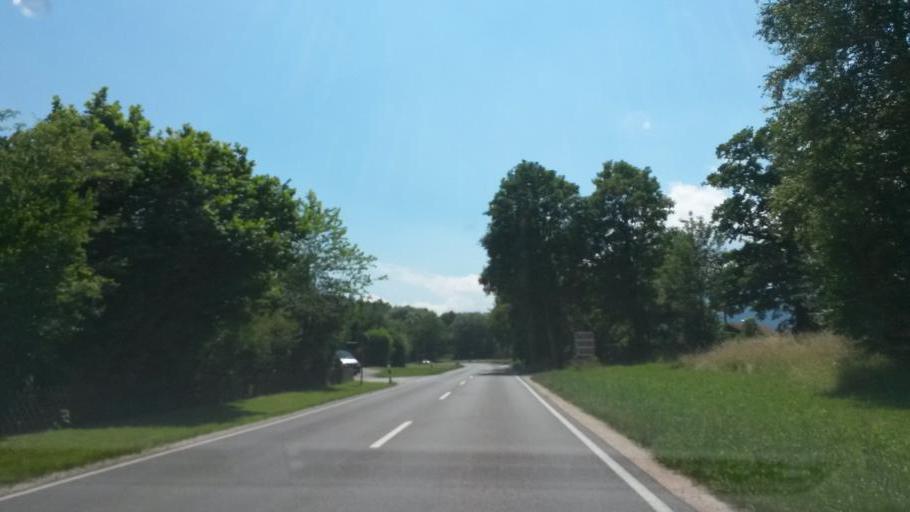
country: DE
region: Bavaria
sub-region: Upper Bavaria
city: Ubersee
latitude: 47.8143
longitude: 12.4924
